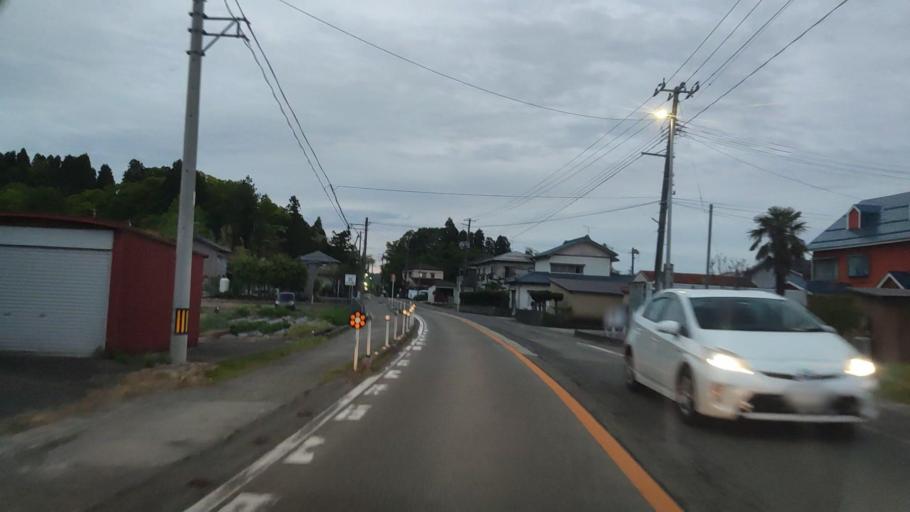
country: JP
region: Niigata
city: Kamo
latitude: 37.7160
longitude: 139.0733
